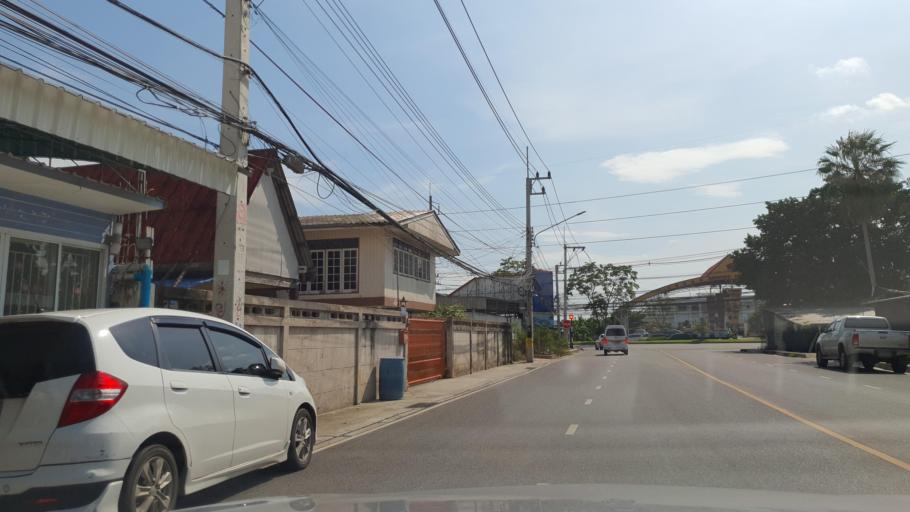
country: TH
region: Chachoengsao
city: Chachoengsao
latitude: 13.6757
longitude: 101.0527
